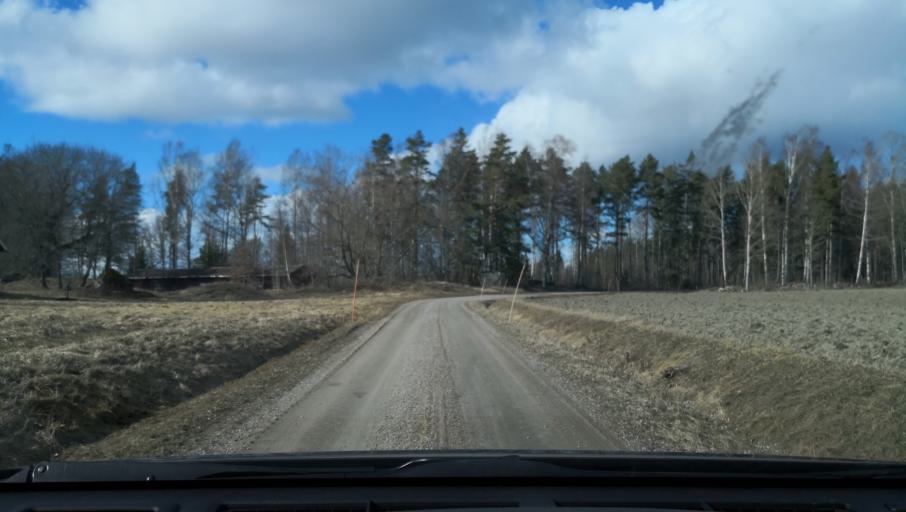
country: SE
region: OErebro
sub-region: Lindesbergs Kommun
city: Fellingsbro
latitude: 59.4268
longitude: 15.6865
